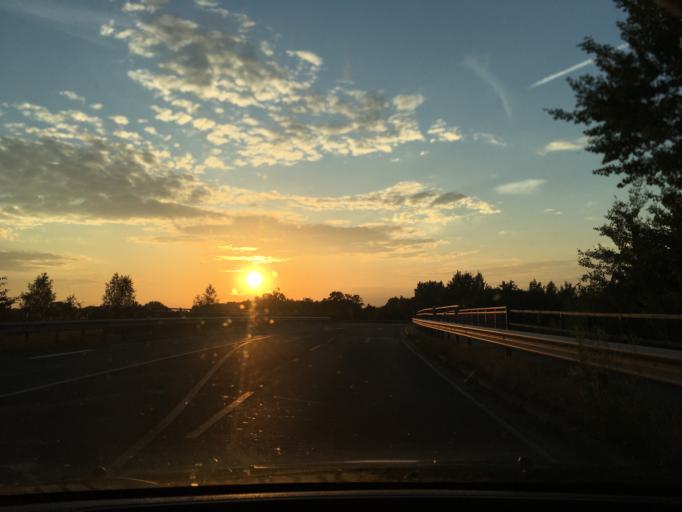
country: DE
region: Lower Saxony
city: Wrestedt
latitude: 52.9164
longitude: 10.5311
